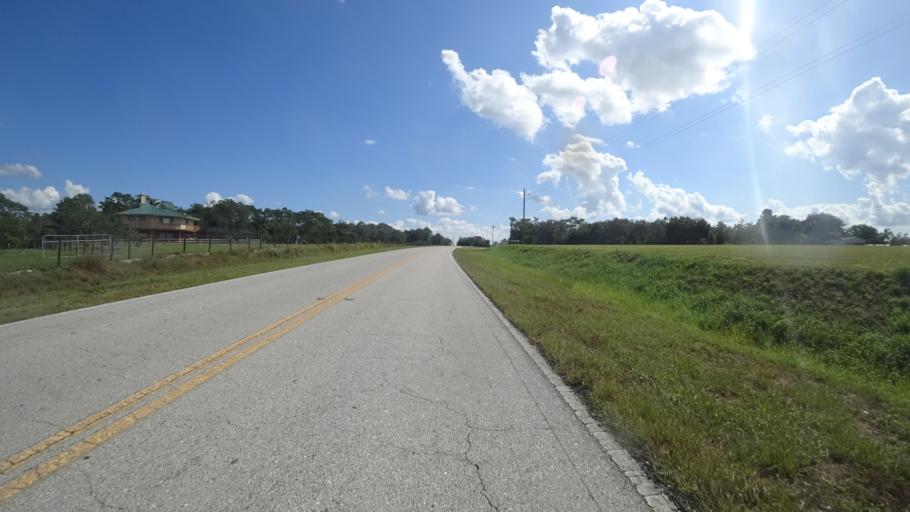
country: US
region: Florida
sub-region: Sarasota County
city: The Meadows
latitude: 27.4697
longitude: -82.3045
